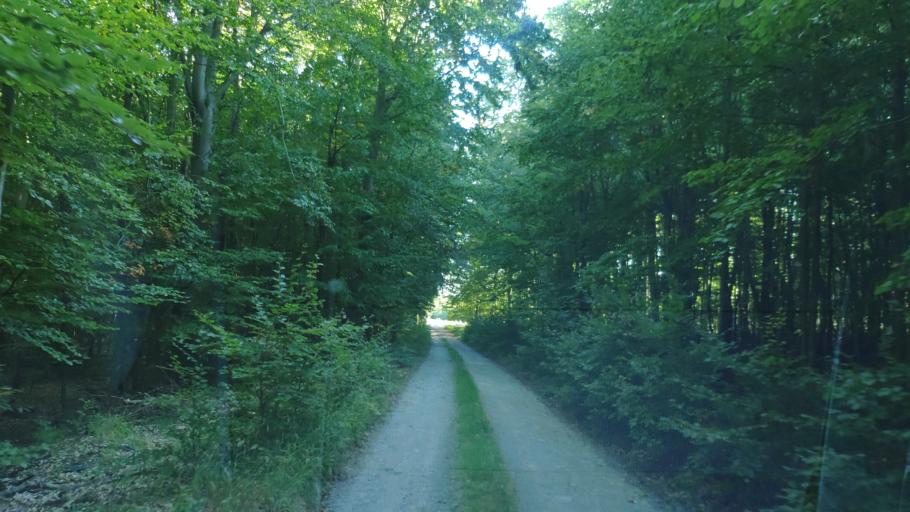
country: SK
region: Presovsky
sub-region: Okres Presov
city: Presov
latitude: 48.8813
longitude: 21.1971
